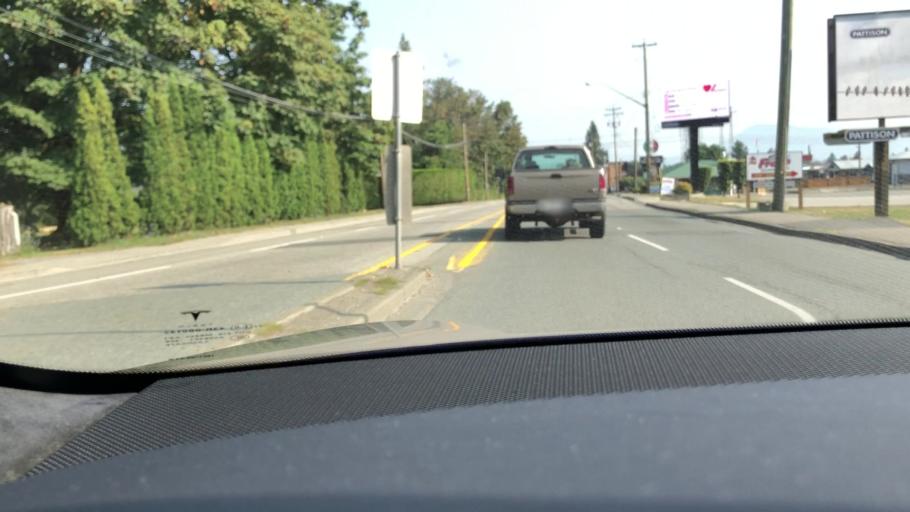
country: CA
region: British Columbia
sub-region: Fraser Valley Regional District
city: Chilliwack
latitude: 49.1120
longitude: -121.9578
